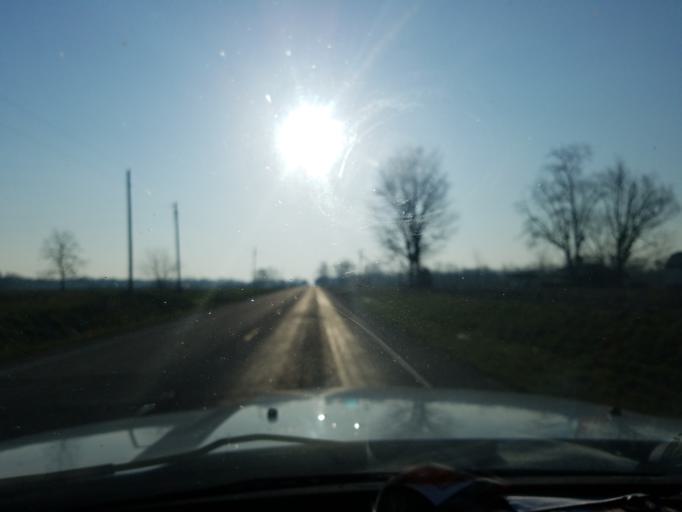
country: US
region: Indiana
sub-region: Vigo County
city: Seelyville
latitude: 39.3885
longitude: -87.1841
